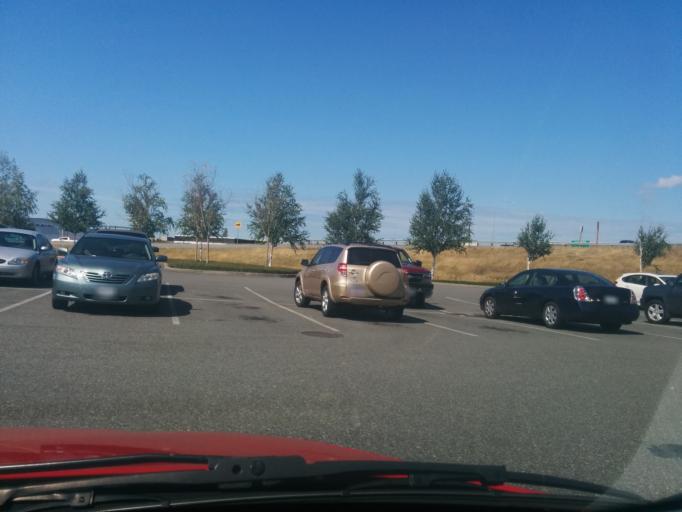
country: US
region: Washington
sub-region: Skagit County
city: Burlington
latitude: 48.4512
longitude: -122.3395
